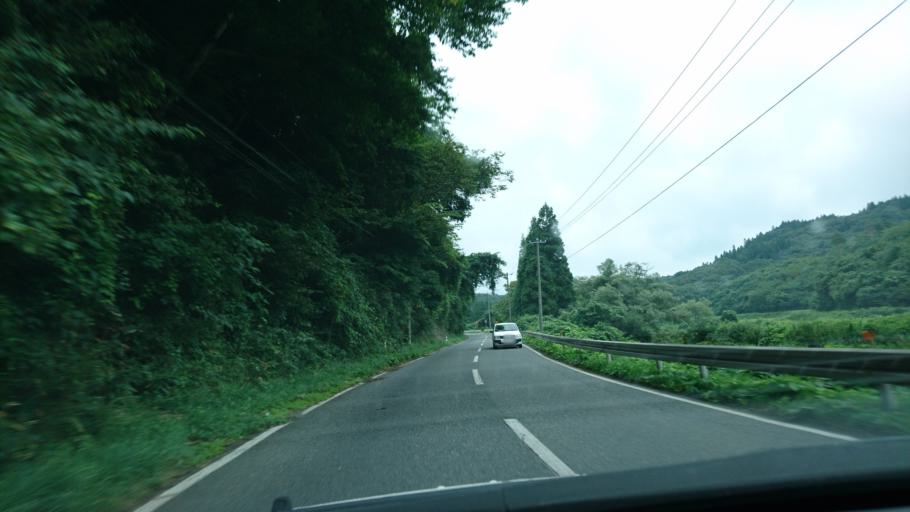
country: JP
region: Iwate
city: Ichinoseki
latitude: 38.9104
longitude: 141.0582
